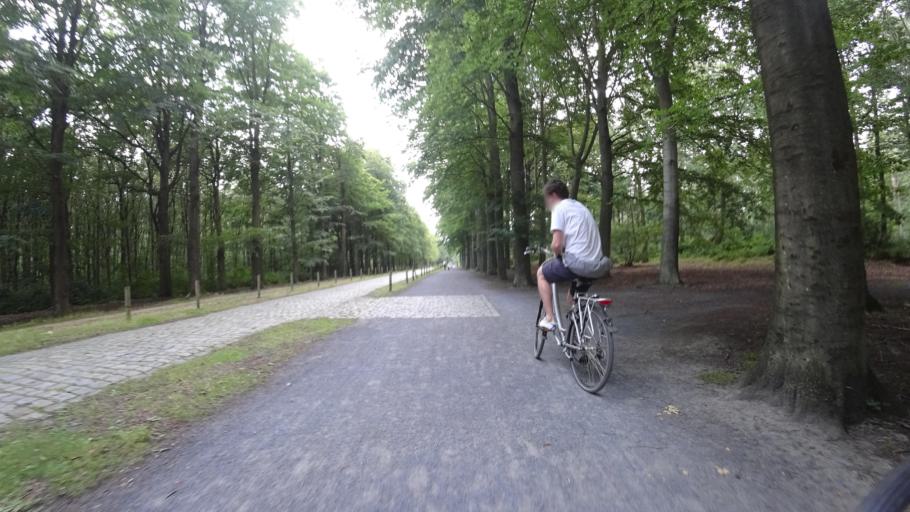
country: BE
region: Flanders
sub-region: Provincie West-Vlaanderen
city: Sint-Kruis
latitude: 51.1984
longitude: 3.2951
